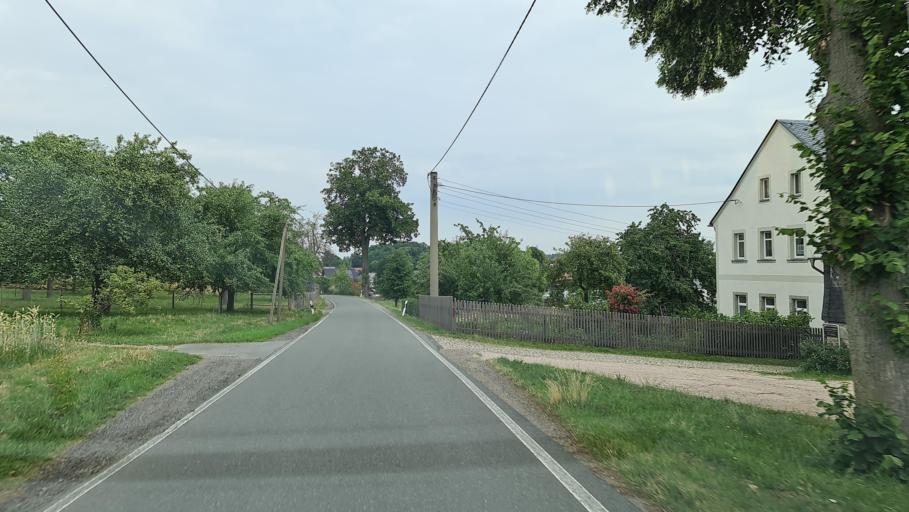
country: DE
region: Saxony
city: Hirschfeld
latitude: 50.5801
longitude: 12.4461
